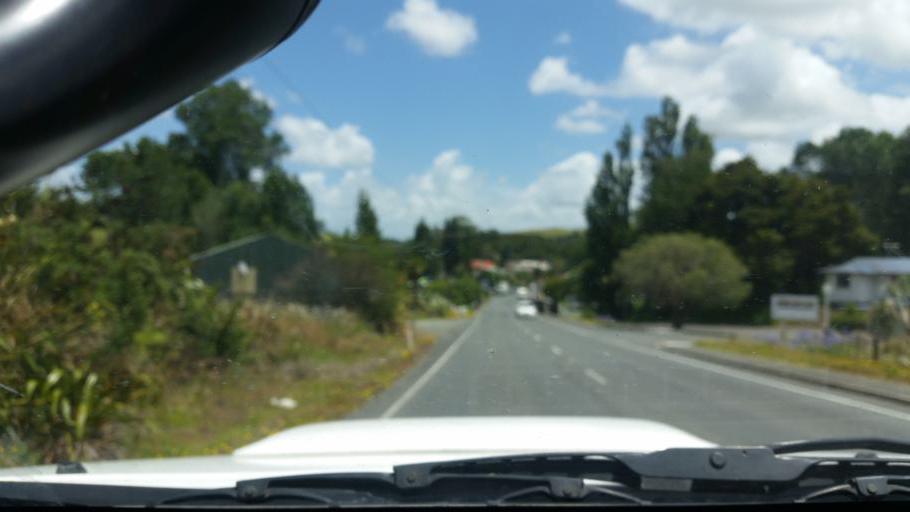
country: NZ
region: Northland
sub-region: Whangarei
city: Ruakaka
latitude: -36.0990
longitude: 174.2373
